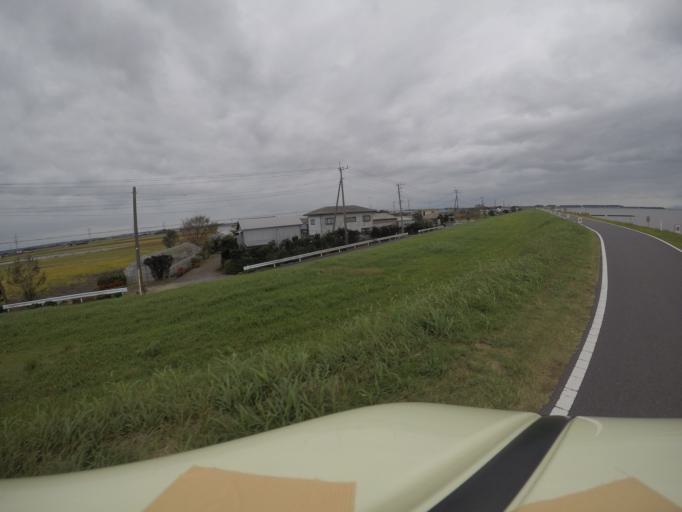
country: JP
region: Chiba
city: Katori-shi
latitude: 35.9572
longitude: 140.4833
